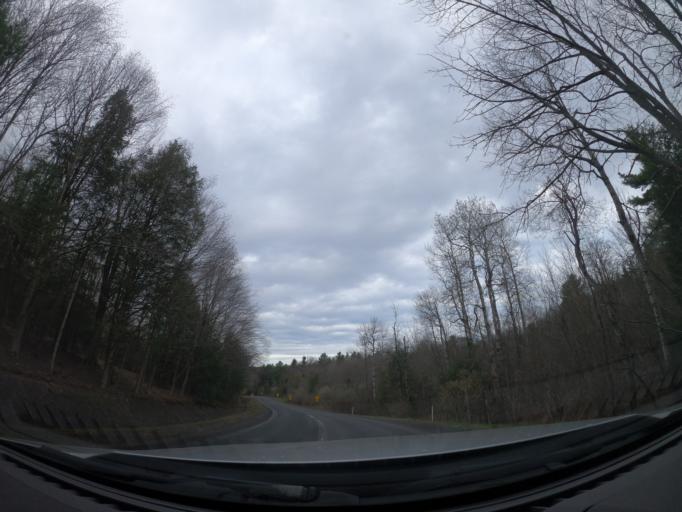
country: US
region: New York
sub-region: Madison County
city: Cazenovia
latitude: 42.8407
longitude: -75.7843
